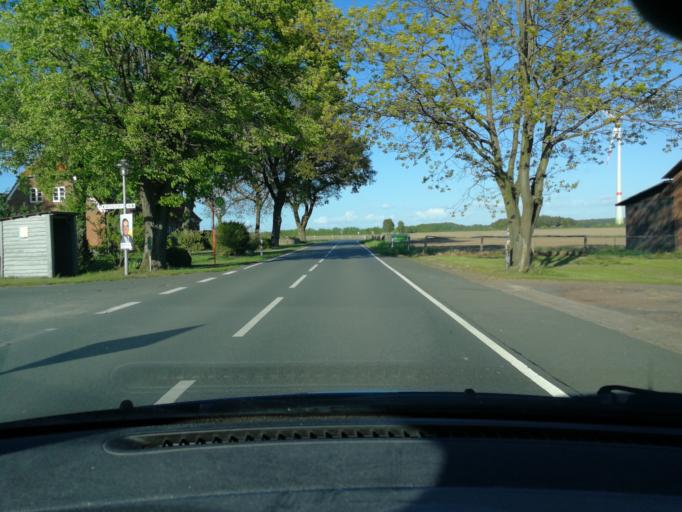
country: DE
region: Lower Saxony
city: Betzendorf
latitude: 53.1027
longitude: 10.2768
